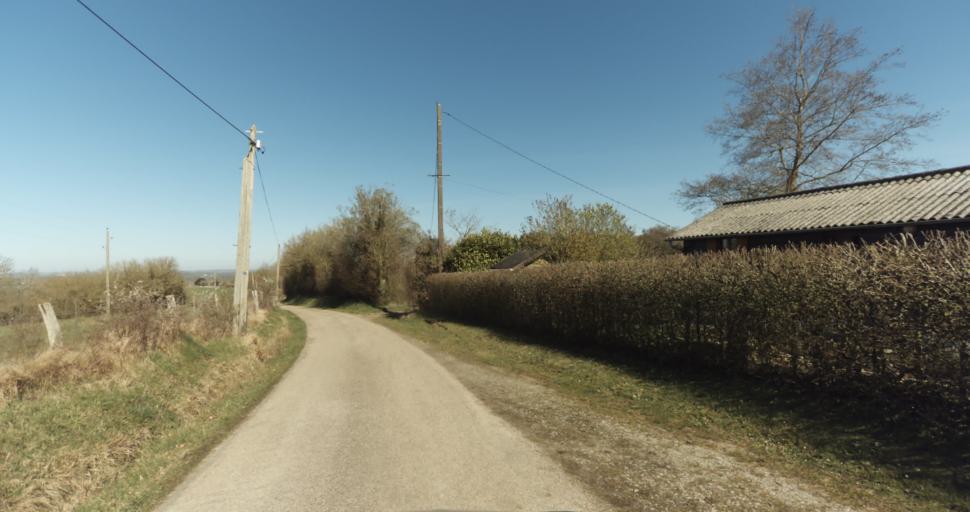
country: FR
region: Lower Normandy
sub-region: Departement de l'Orne
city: Trun
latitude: 48.9218
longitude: 0.0571
